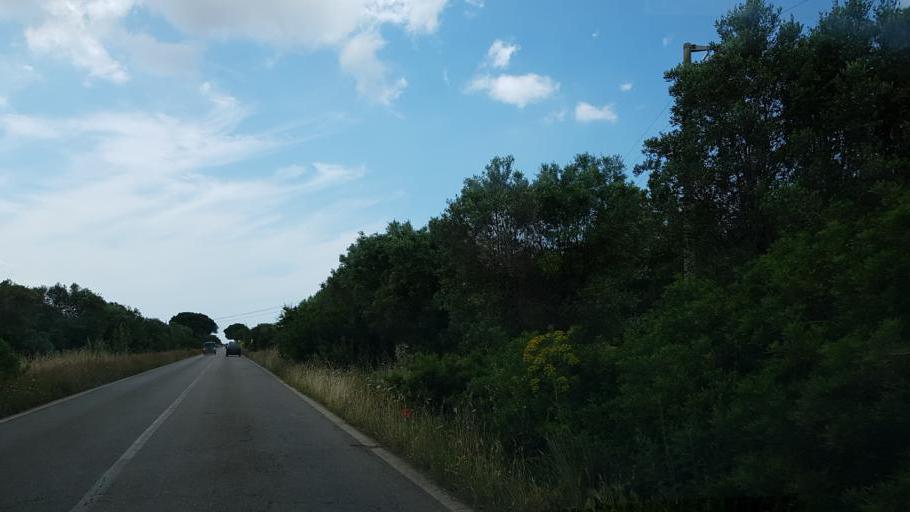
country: IT
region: Apulia
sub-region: Provincia di Brindisi
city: San Pancrazio Salentino
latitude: 40.3476
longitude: 17.8467
